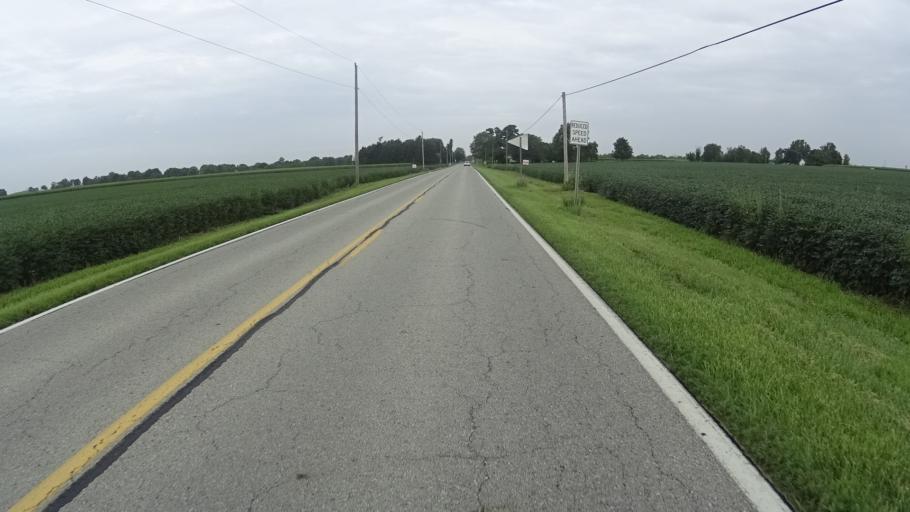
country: US
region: Indiana
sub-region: Madison County
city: Lapel
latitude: 40.0562
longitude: -85.8311
